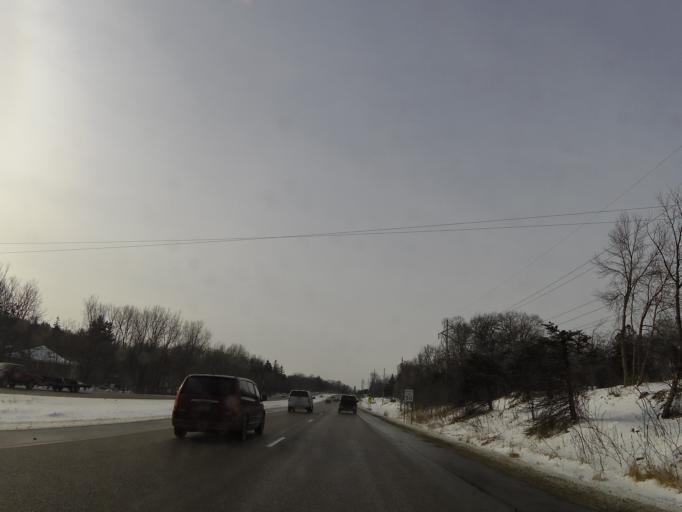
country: US
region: Minnesota
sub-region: Hennepin County
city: Excelsior
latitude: 44.8965
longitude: -93.5708
